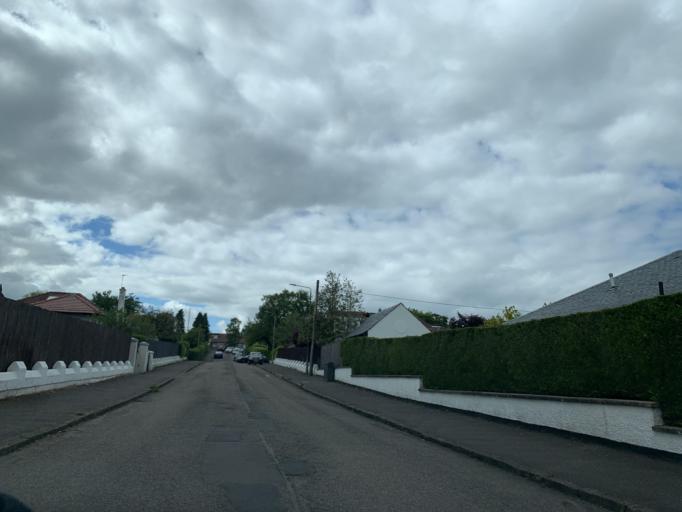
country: GB
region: Scotland
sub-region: East Renfrewshire
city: Newton Mearns
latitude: 55.7732
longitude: -4.3270
